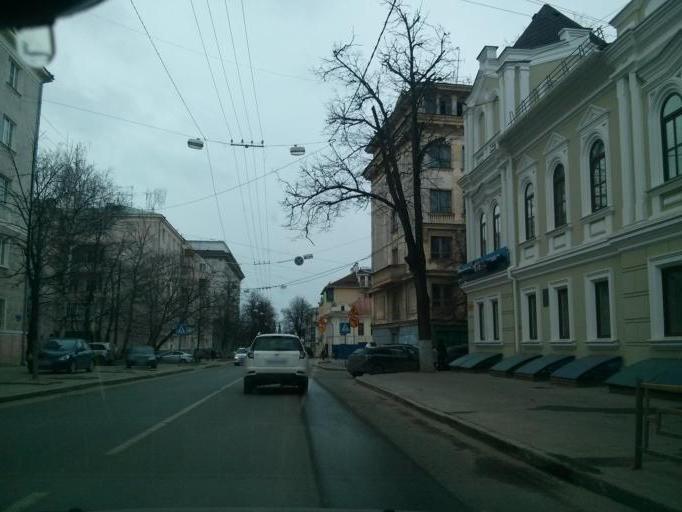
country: RU
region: Nizjnij Novgorod
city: Nizhniy Novgorod
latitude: 56.3287
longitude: 44.0127
